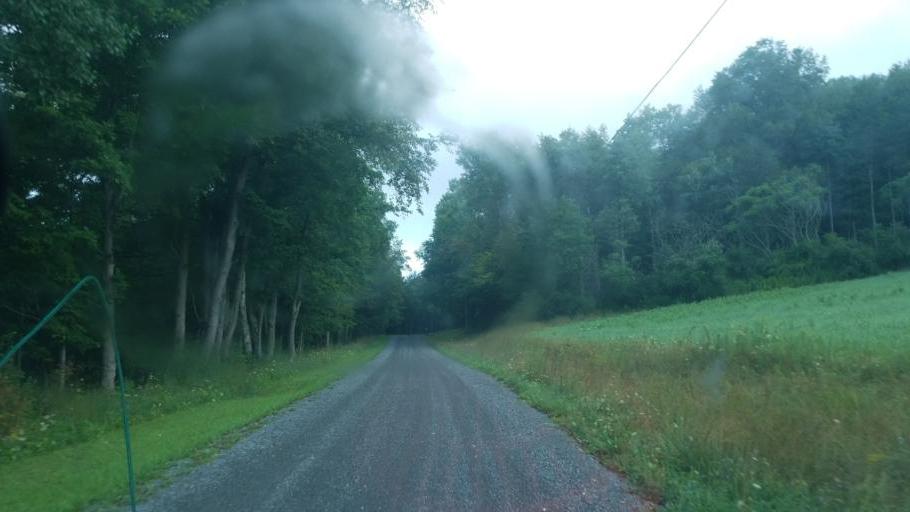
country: US
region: Pennsylvania
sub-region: Potter County
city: Galeton
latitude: 41.8382
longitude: -77.7950
